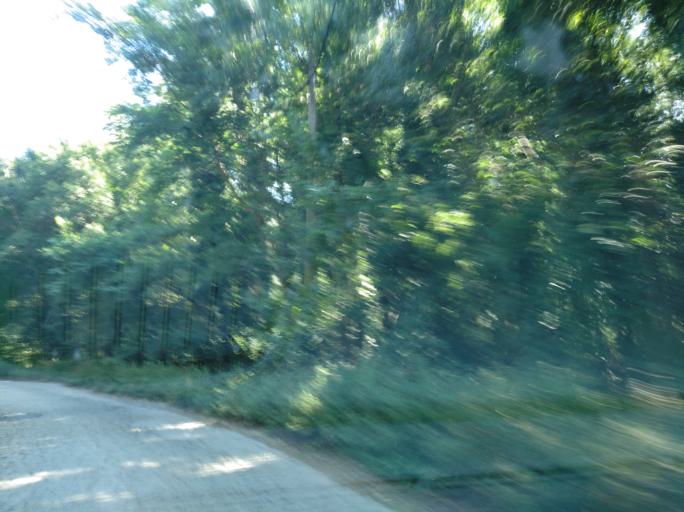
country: ES
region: Catalonia
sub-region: Provincia de Girona
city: la Cellera de Ter
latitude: 41.9769
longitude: 2.6002
